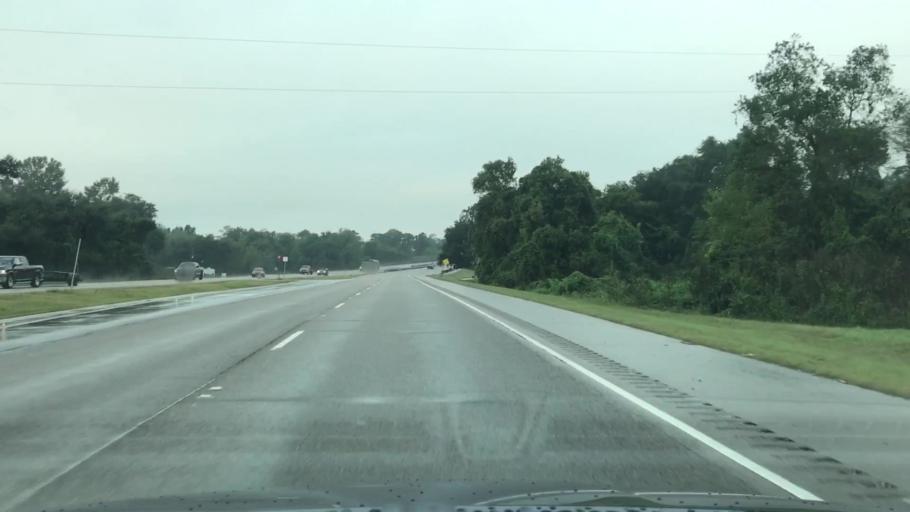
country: US
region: Louisiana
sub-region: Saint Charles Parish
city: Des Allemands
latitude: 29.8228
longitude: -90.4702
